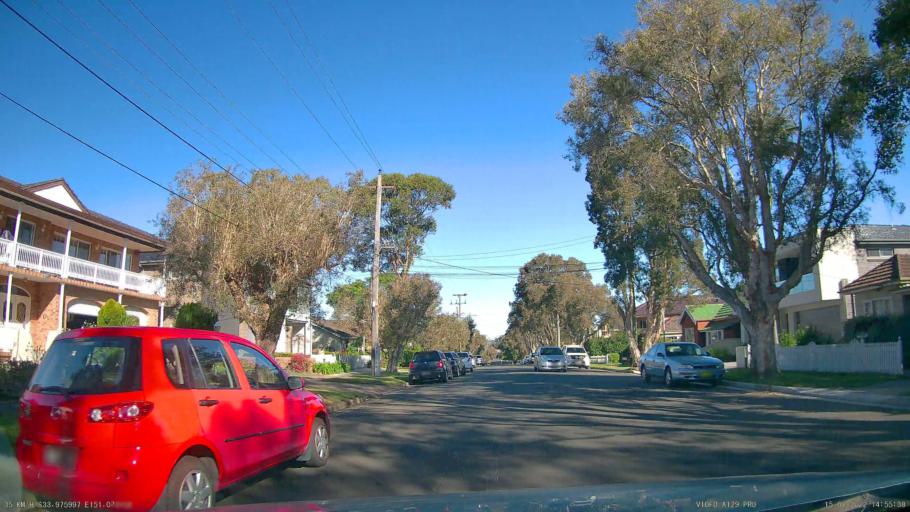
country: AU
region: New South Wales
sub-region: Hurstville
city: Oatley
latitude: -33.9761
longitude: 151.0721
